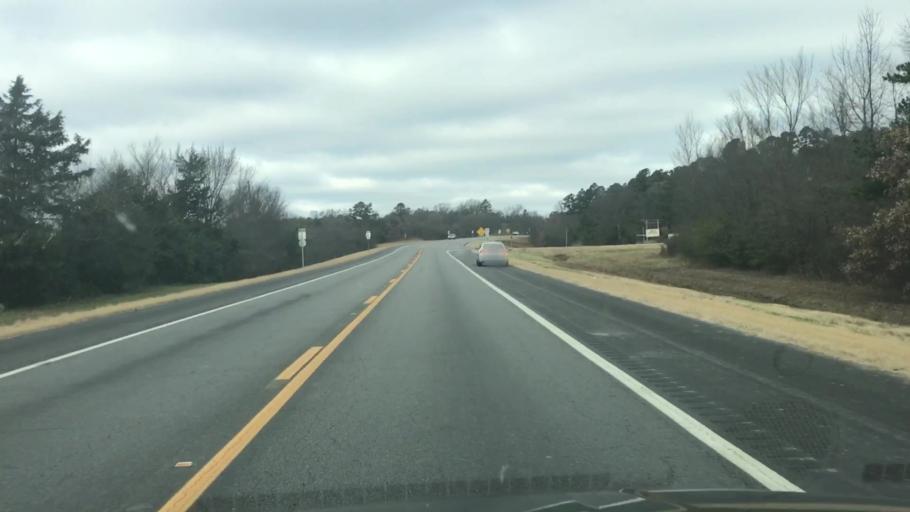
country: US
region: Arkansas
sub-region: Scott County
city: Waldron
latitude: 34.8812
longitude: -94.1023
